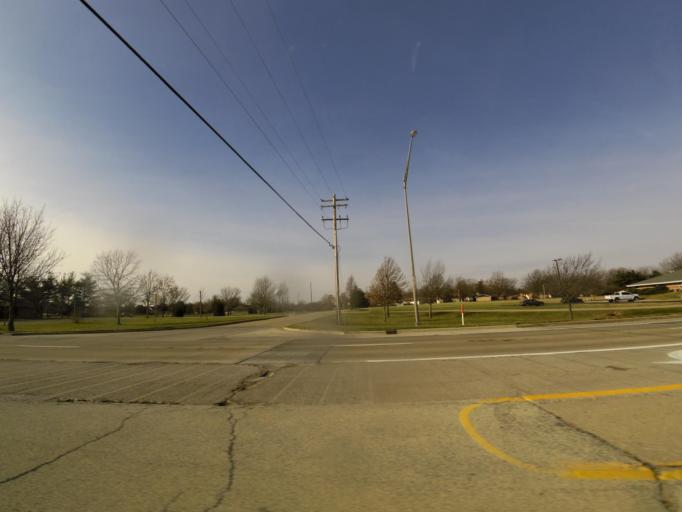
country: US
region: Illinois
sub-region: Macon County
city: Forsyth
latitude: 39.9324
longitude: -88.9556
